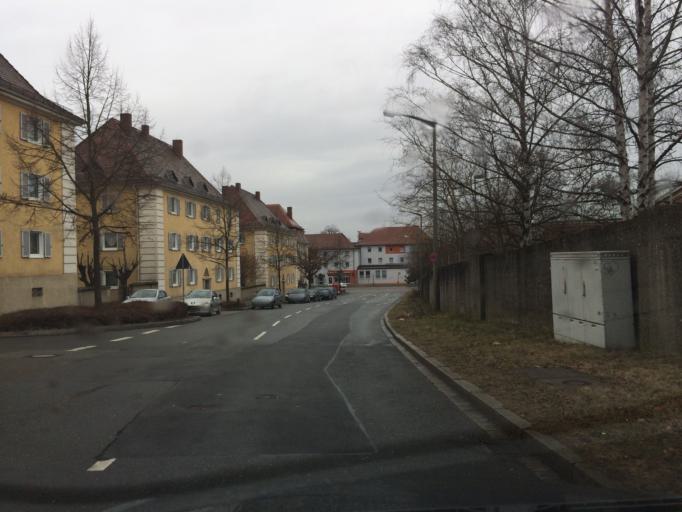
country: DE
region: Bavaria
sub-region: Regierungsbezirk Mittelfranken
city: Nuernberg
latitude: 49.4291
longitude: 11.0938
